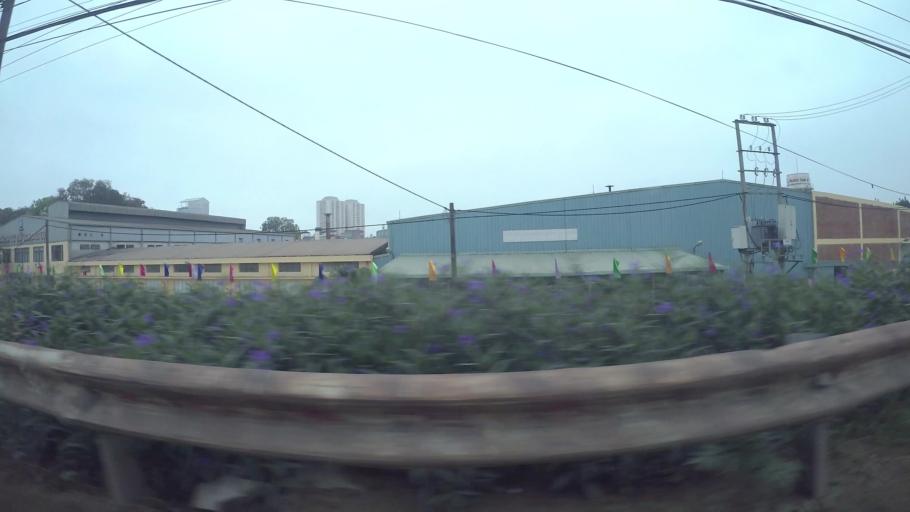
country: VN
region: Ha Noi
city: Hai BaTrung
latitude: 20.9958
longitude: 105.8924
